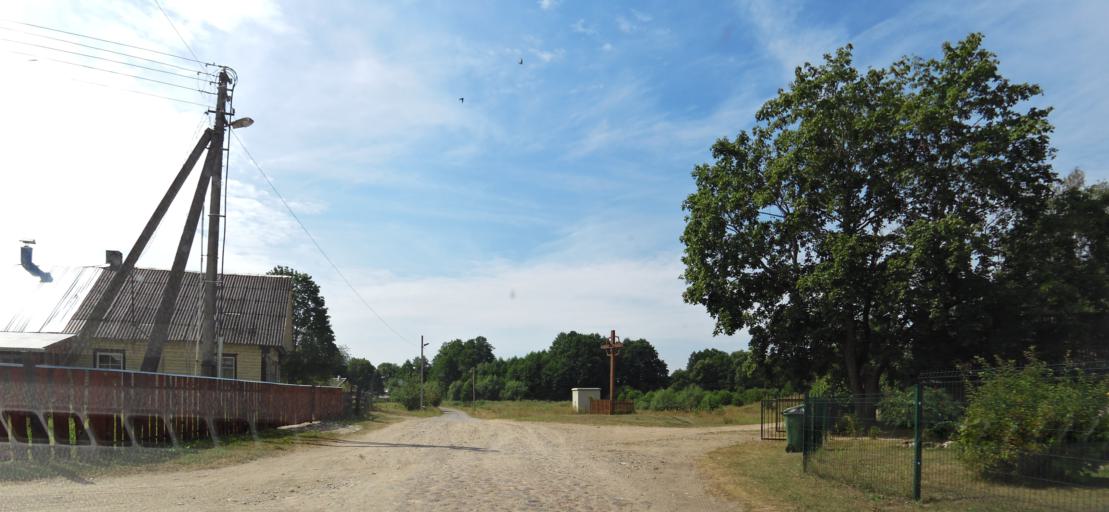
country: LT
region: Vilnius County
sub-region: Trakai
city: Rudiskes
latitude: 54.3639
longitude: 24.8450
